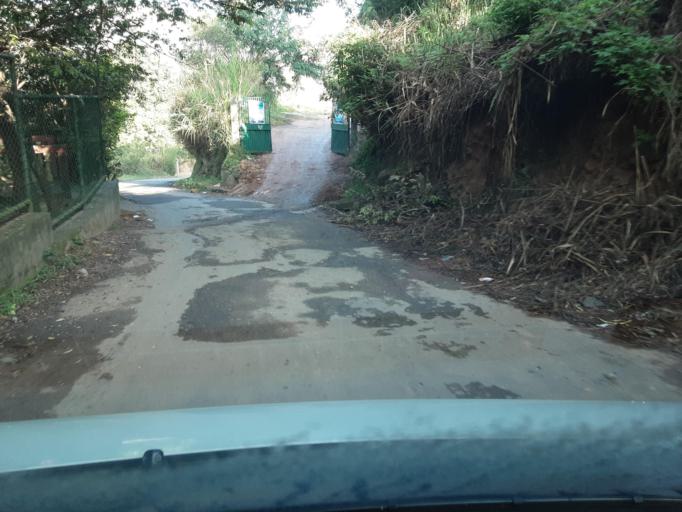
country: LK
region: Uva
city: Haputale
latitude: 6.9060
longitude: 80.9196
